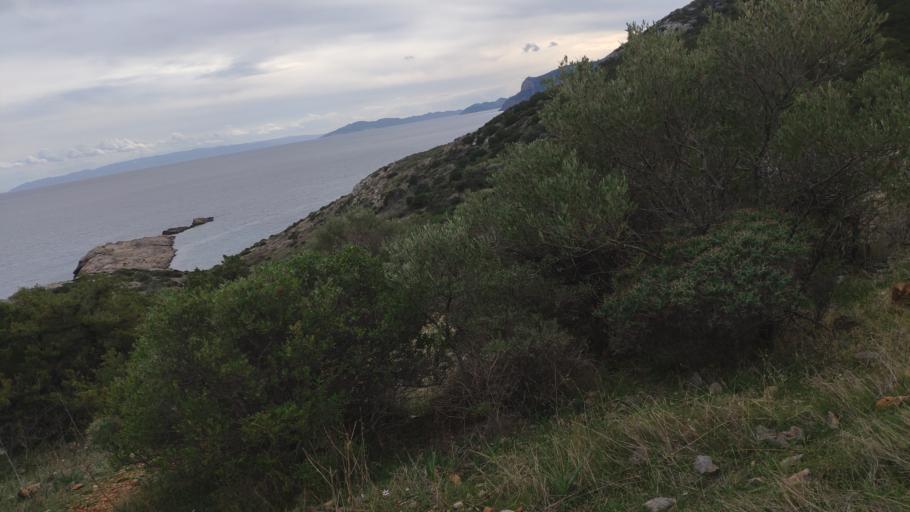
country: GR
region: Attica
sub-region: Nomarchia Anatolikis Attikis
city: Limin Mesoyaias
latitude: 37.9049
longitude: 24.0429
